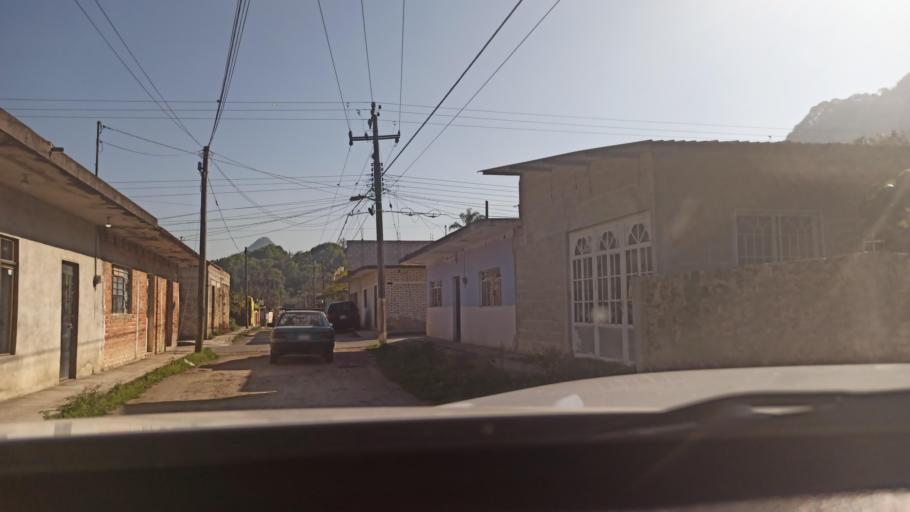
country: MX
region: Veracruz
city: Atzacan
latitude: 18.9101
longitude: -97.0869
